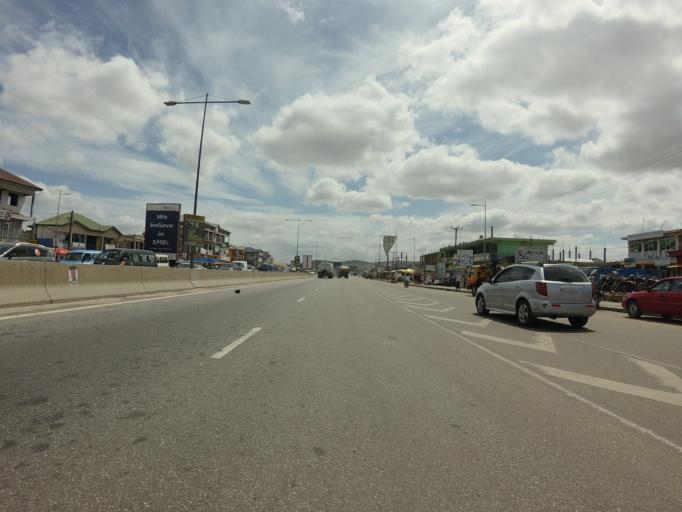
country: GH
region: Central
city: Kasoa
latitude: 5.5352
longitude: -0.4205
